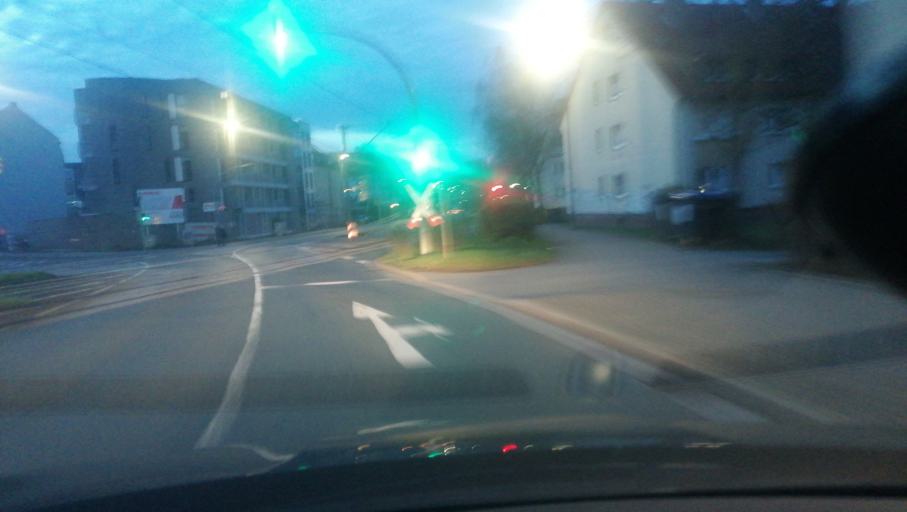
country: DE
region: North Rhine-Westphalia
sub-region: Regierungsbezirk Arnsberg
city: Dortmund
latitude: 51.5313
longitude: 7.4193
